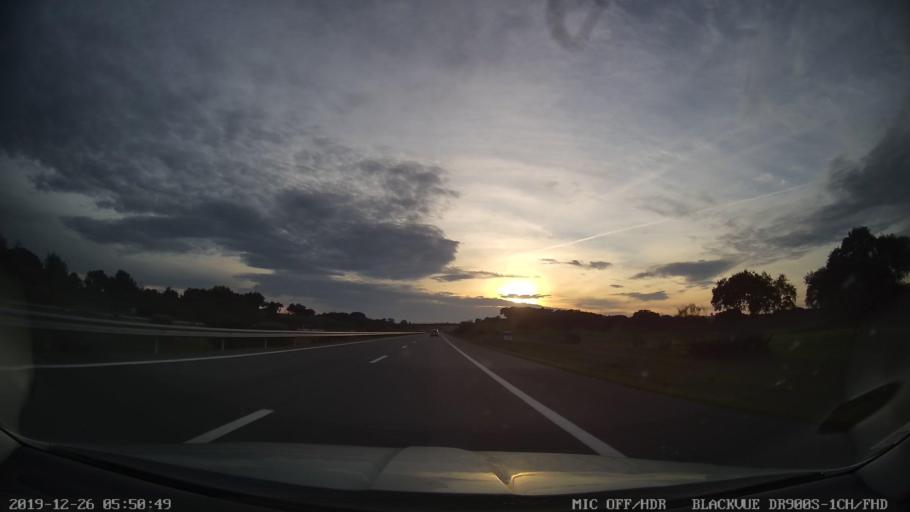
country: PT
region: Evora
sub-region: Evora
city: Evora
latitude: 38.6729
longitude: -7.8300
